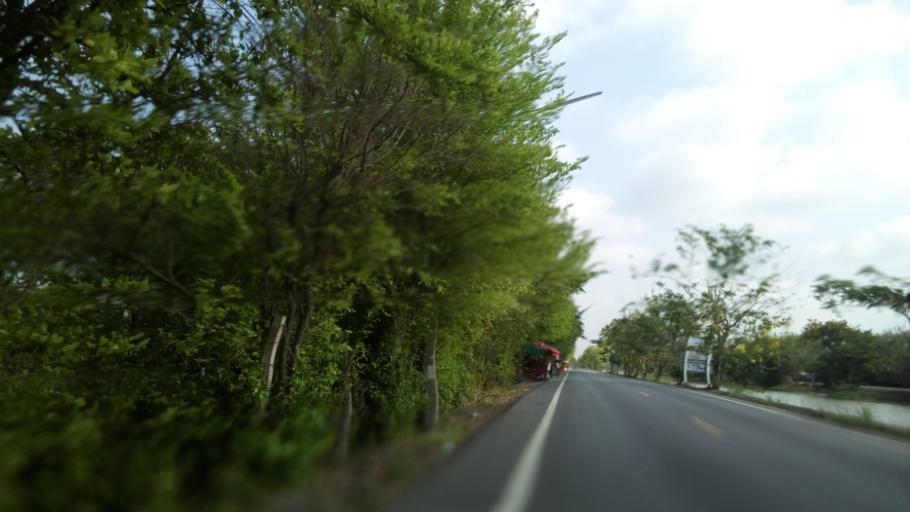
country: TH
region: Pathum Thani
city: Nong Suea
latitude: 14.1381
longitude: 100.8459
